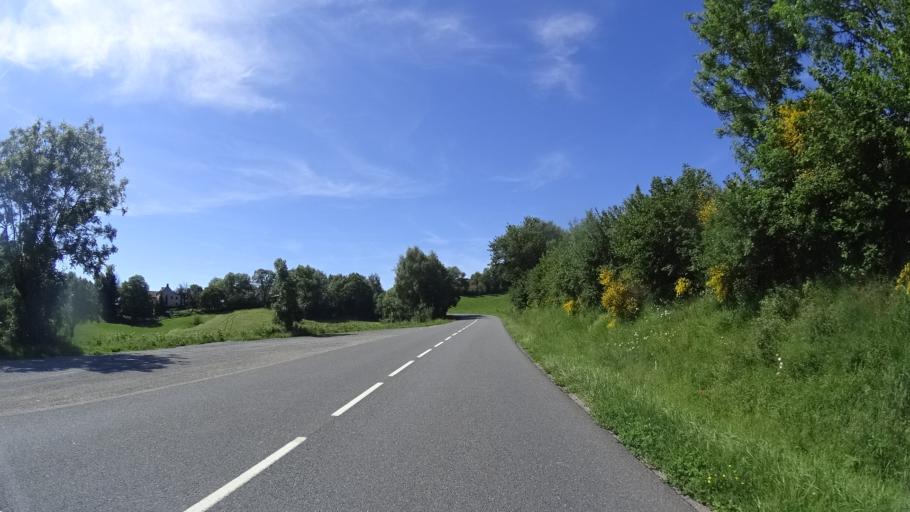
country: FR
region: Midi-Pyrenees
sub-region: Departement de l'Aveyron
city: Pont-de-Salars
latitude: 44.3306
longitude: 2.7733
